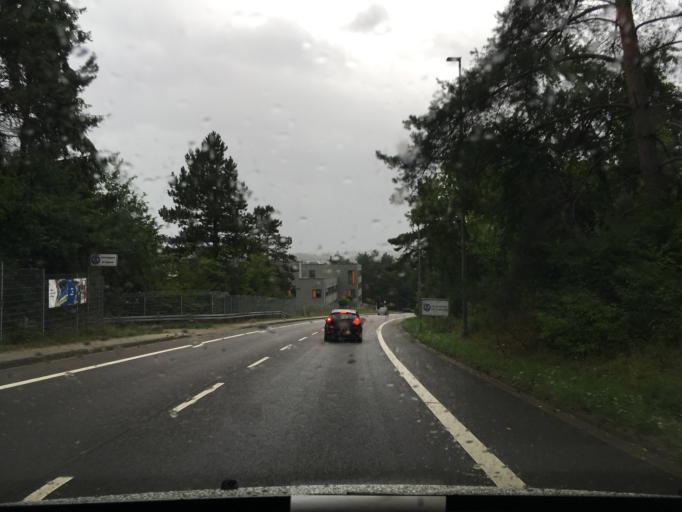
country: DE
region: Saarland
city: Sankt Ingbert
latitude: 49.2811
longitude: 7.1316
